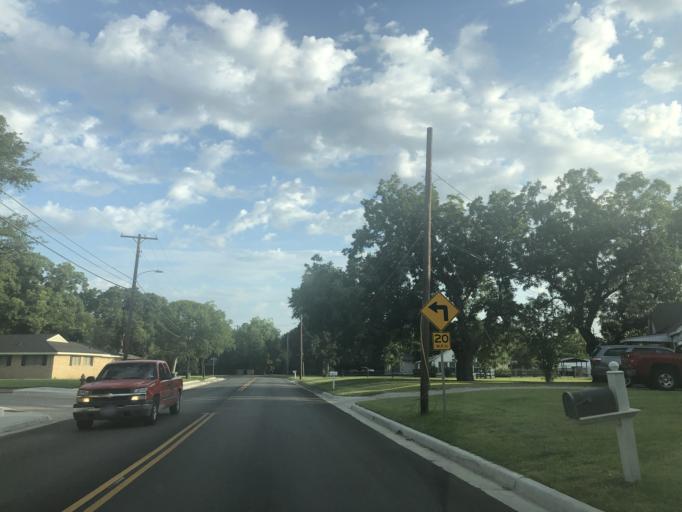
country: US
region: Texas
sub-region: Dallas County
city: Grand Prairie
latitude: 32.7631
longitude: -97.0124
